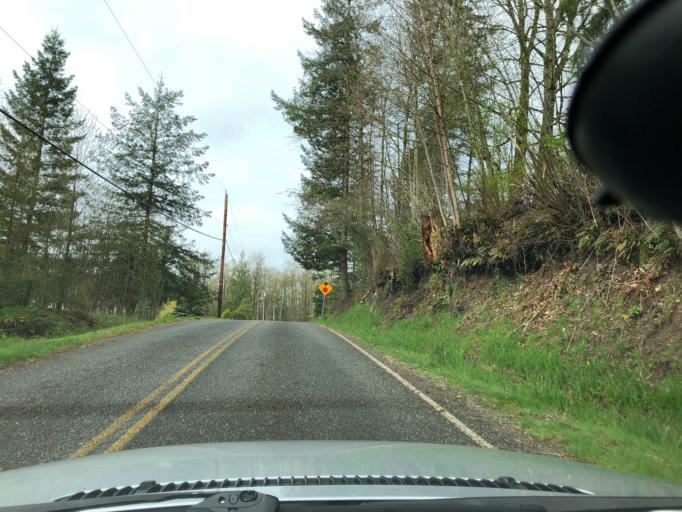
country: CA
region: British Columbia
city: Langley
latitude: 48.9786
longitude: -122.6136
